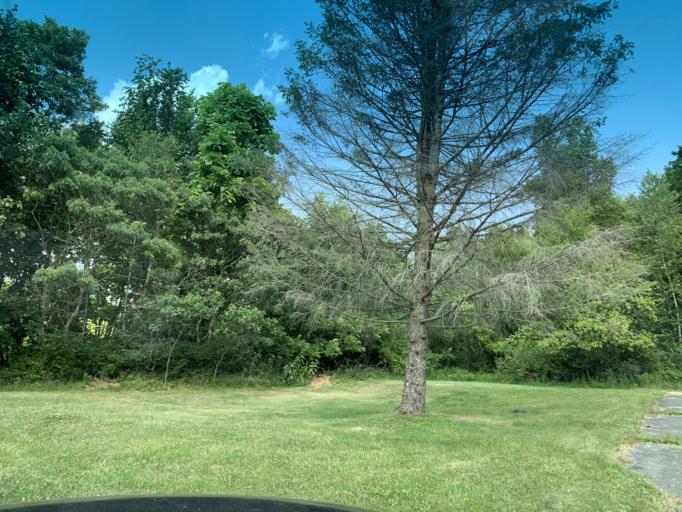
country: US
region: Pennsylvania
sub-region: Schuylkill County
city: Ashland
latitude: 40.8024
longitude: -76.3372
